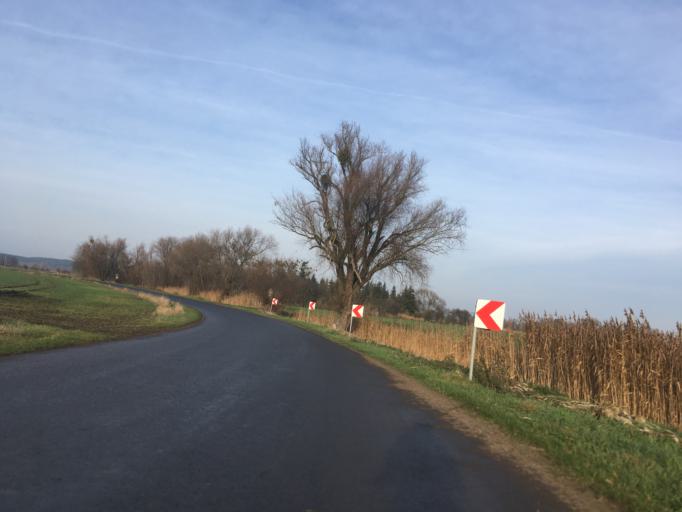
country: DE
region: Brandenburg
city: Bad Freienwalde
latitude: 52.7824
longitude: 14.0834
